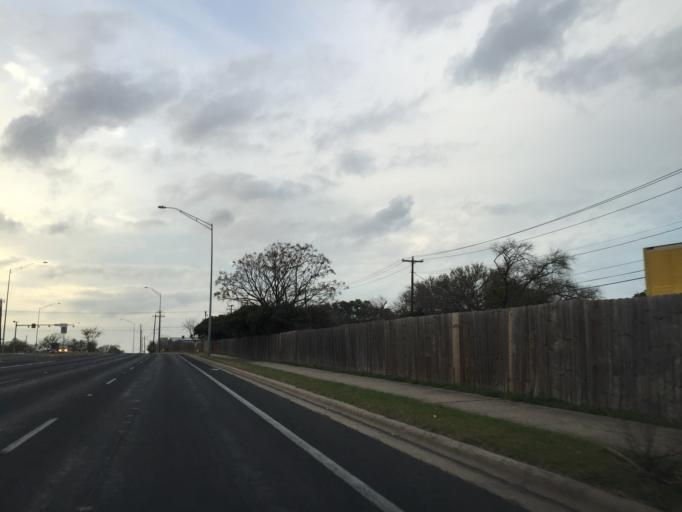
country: US
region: Texas
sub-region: Travis County
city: Wells Branch
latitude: 30.3842
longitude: -97.6912
